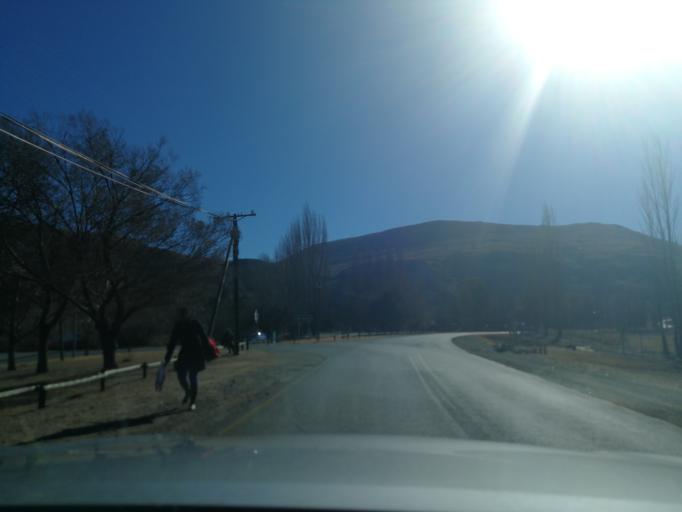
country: ZA
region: Orange Free State
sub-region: Thabo Mofutsanyana District Municipality
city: Bethlehem
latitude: -28.5110
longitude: 28.4252
